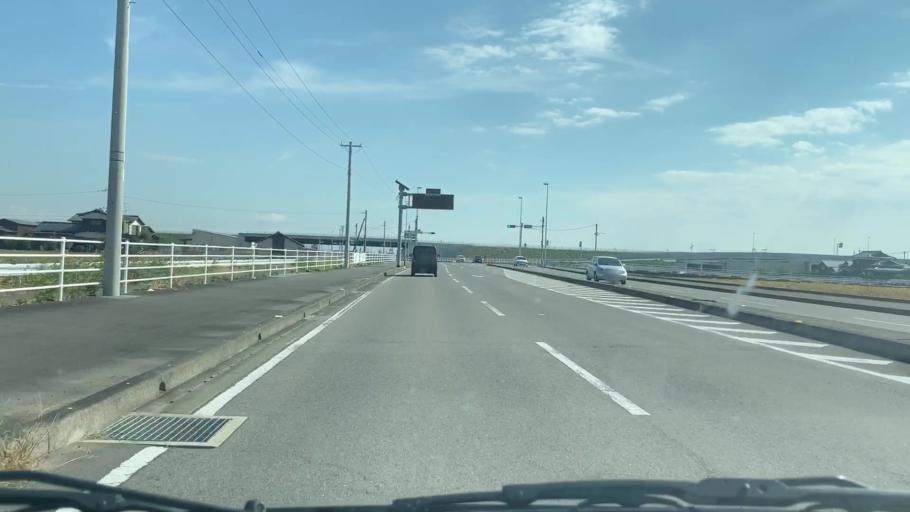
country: JP
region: Saga Prefecture
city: Saga-shi
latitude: 33.2208
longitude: 130.2114
